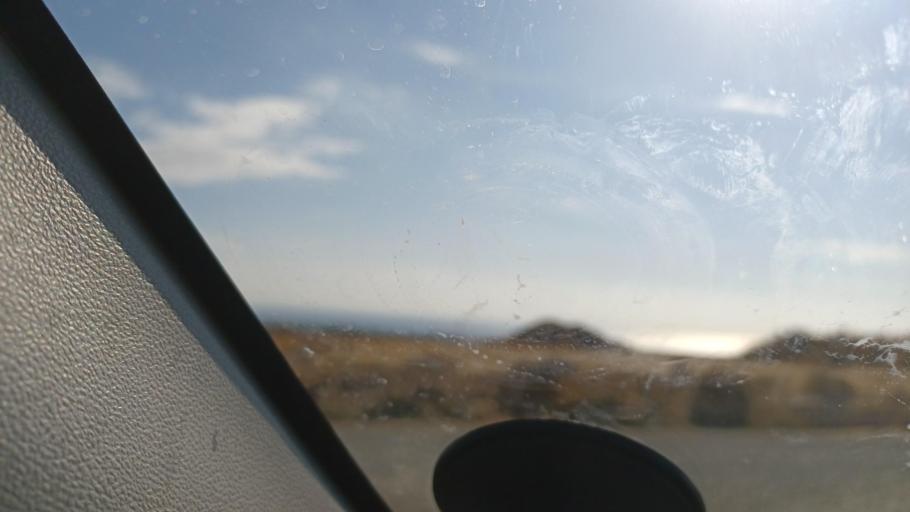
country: CY
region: Pafos
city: Mesogi
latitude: 34.7351
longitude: 32.5504
